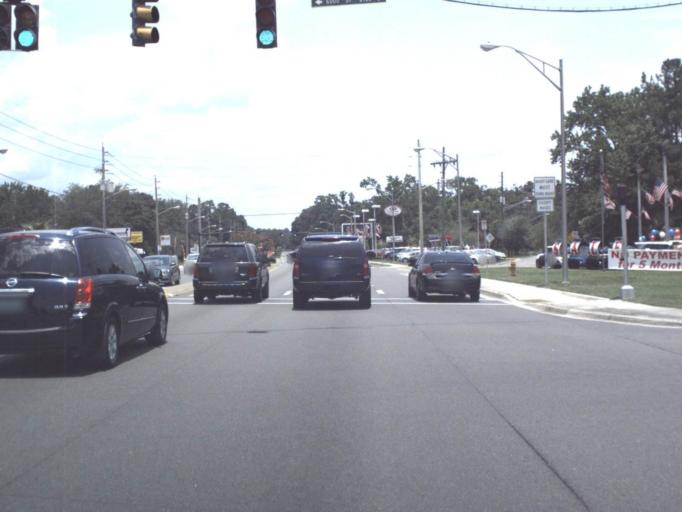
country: US
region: Florida
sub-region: Clay County
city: Bellair-Meadowbrook Terrace
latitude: 30.2337
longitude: -81.7392
